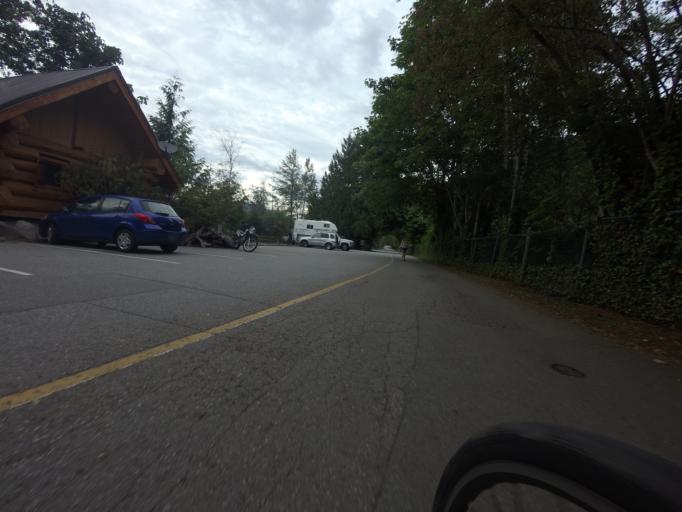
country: CA
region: British Columbia
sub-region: Greater Vancouver Regional District
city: Lions Bay
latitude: 49.5580
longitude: -123.2352
